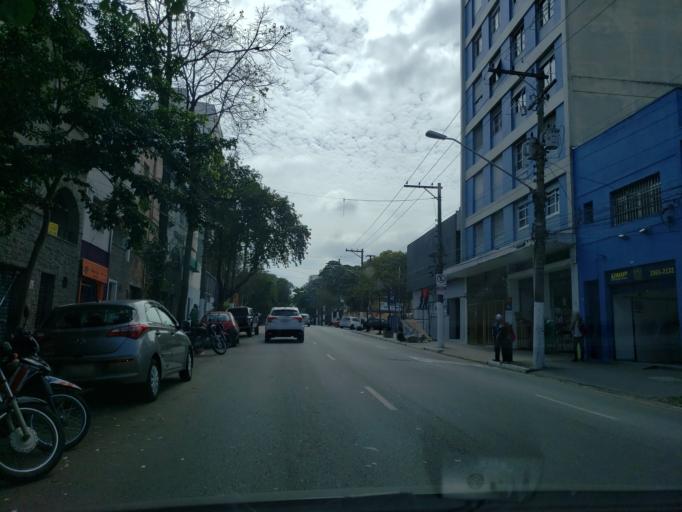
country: BR
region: Sao Paulo
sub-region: Sao Paulo
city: Sao Paulo
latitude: -23.5864
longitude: -46.6075
